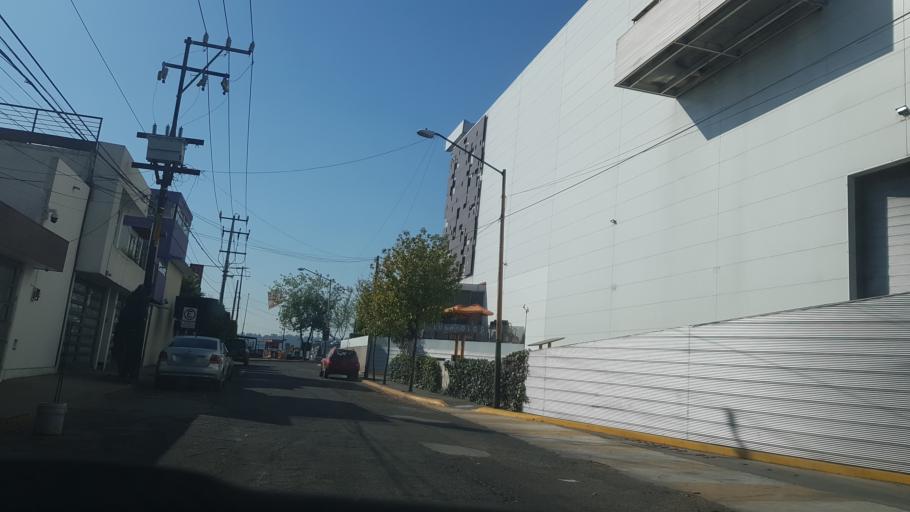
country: MX
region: Mexico
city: Naucalpan de Juarez
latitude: 19.4954
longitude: -99.2462
